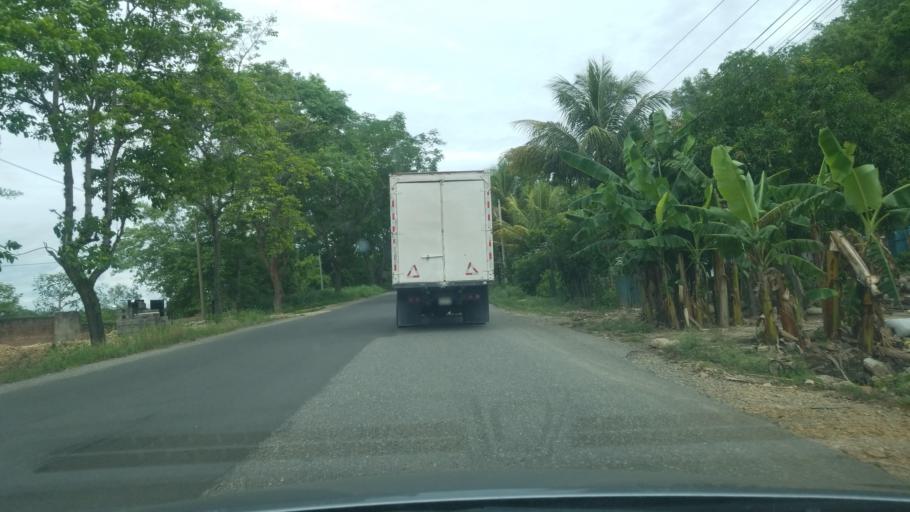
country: HN
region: Santa Barbara
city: San Marcos
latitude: 15.3140
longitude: -88.4330
